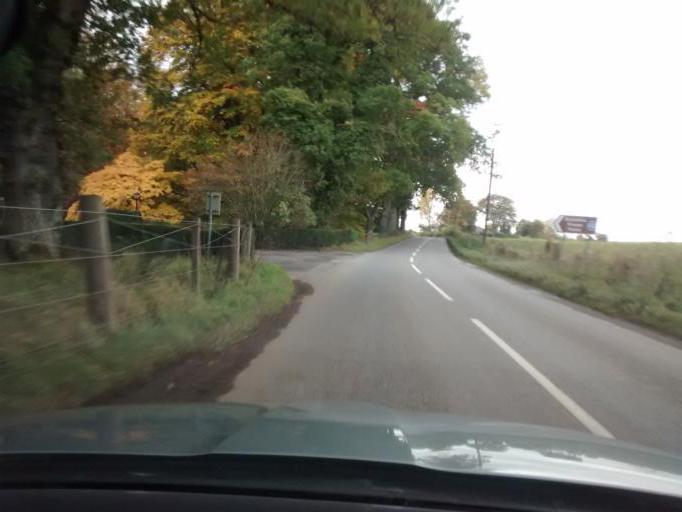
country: GB
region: Scotland
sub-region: Perth and Kinross
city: Stanley
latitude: 56.5155
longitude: -3.4067
